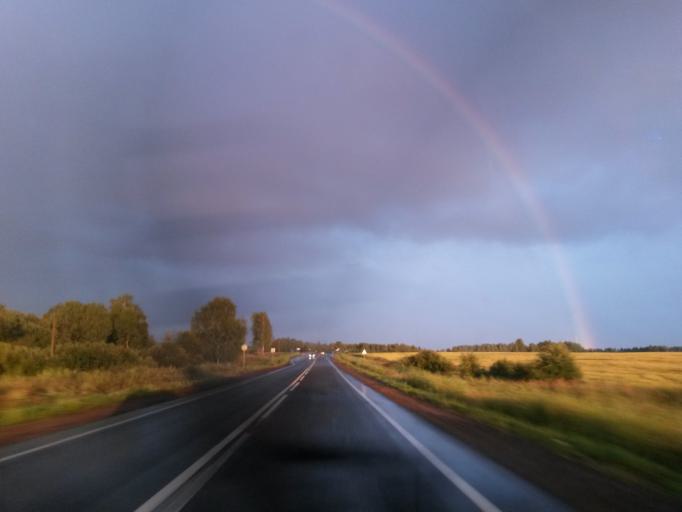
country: RU
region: Jaroslavl
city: Gavrilov-Yam
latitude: 57.3256
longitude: 39.9243
